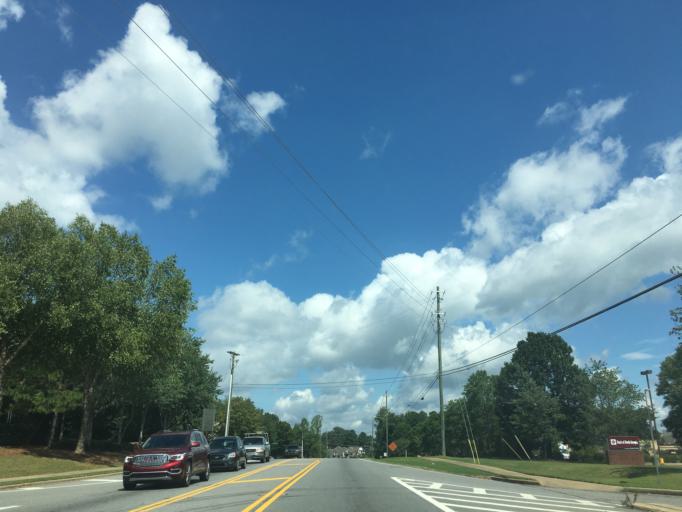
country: US
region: Georgia
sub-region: Fulton County
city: Roswell
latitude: 34.0834
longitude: -84.3581
